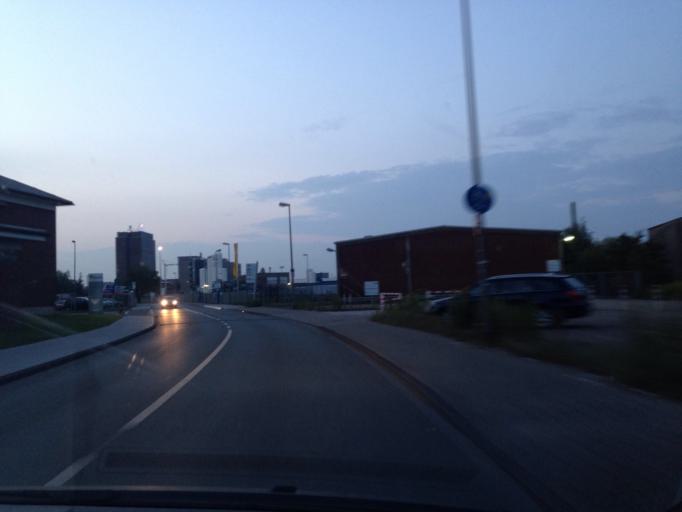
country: DE
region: North Rhine-Westphalia
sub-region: Regierungsbezirk Munster
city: Muenster
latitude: 51.9420
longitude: 7.6362
